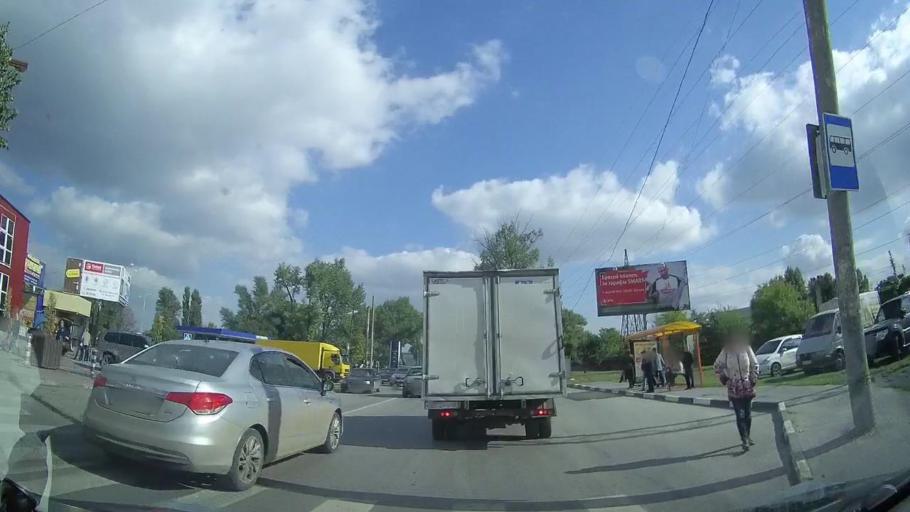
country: RU
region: Rostov
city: Imeni Chkalova
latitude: 47.2663
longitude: 39.7665
